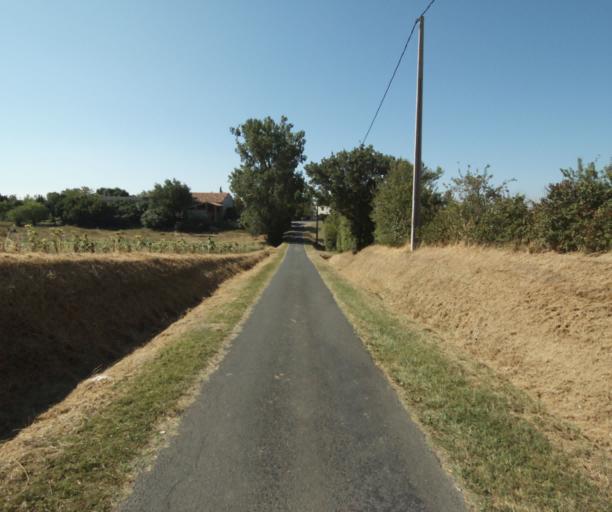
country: FR
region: Midi-Pyrenees
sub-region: Departement de la Haute-Garonne
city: Saint-Felix-Lauragais
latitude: 43.5087
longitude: 1.9244
